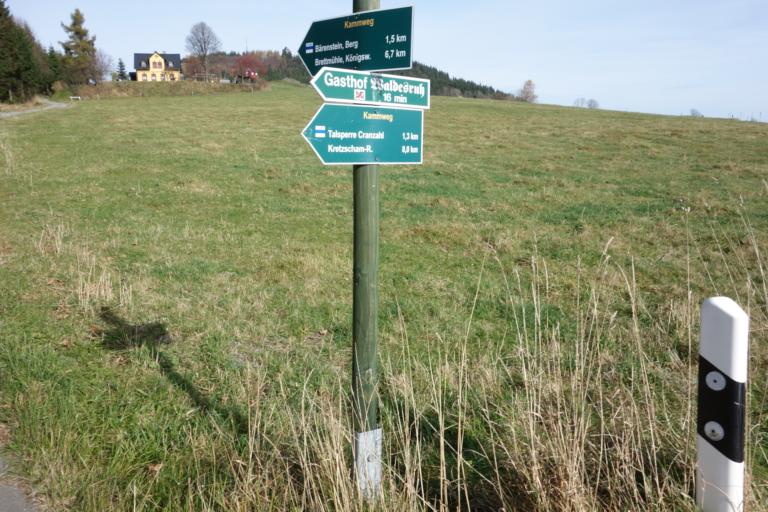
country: DE
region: Saxony
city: Barenstein
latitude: 50.5004
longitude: 13.0166
